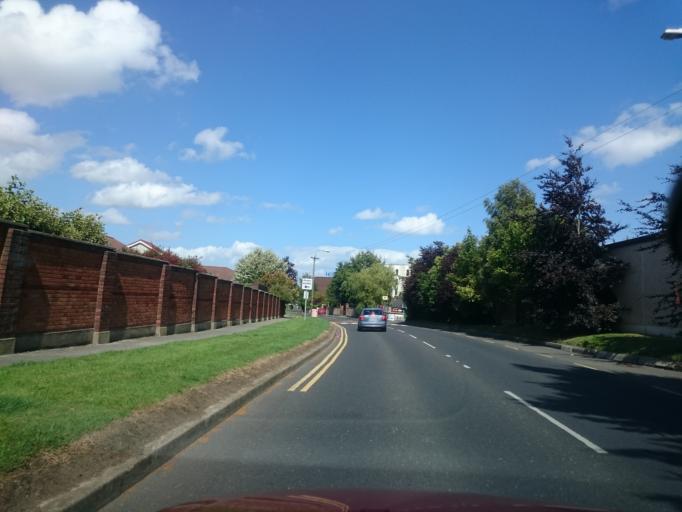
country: IE
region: Leinster
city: Clondalkin
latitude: 53.3084
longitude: -6.4056
